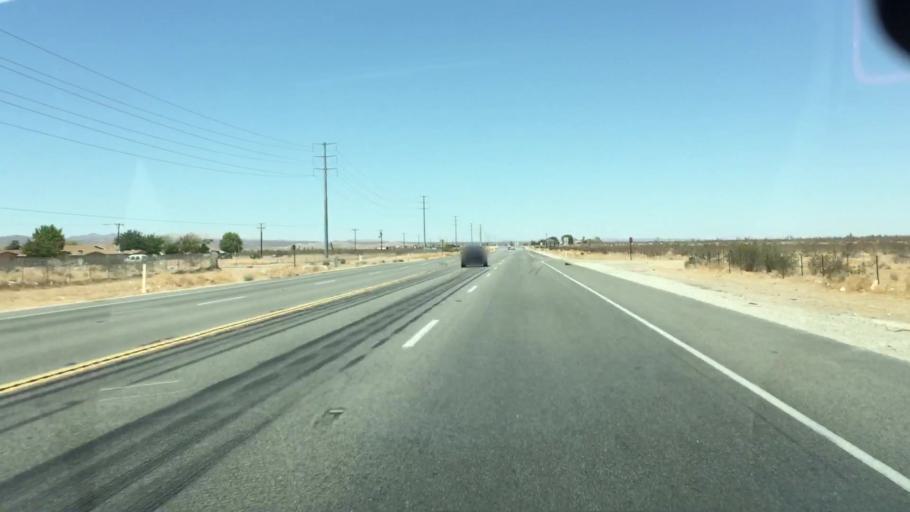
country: US
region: California
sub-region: San Bernardino County
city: Adelanto
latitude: 34.5928
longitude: -117.4166
